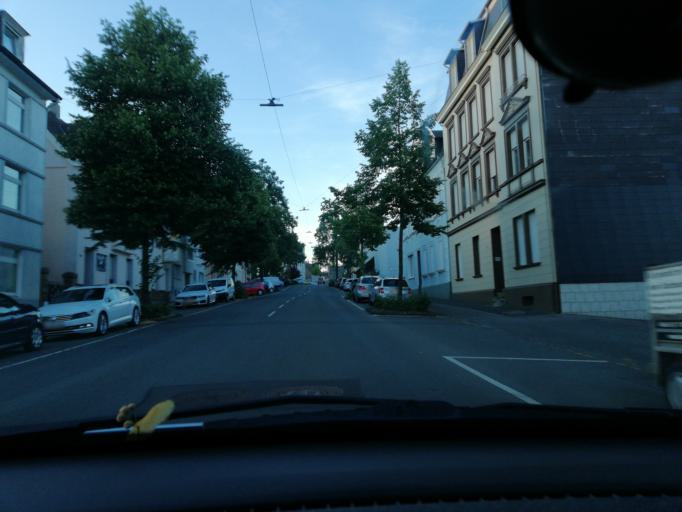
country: DE
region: North Rhine-Westphalia
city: Sprockhovel
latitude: 51.2937
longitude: 7.2386
